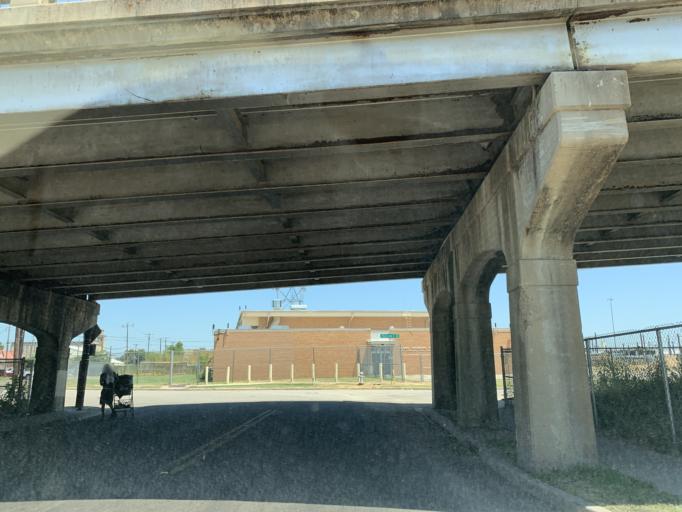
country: US
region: Texas
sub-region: Dallas County
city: Dallas
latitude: 32.7770
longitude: -96.7772
